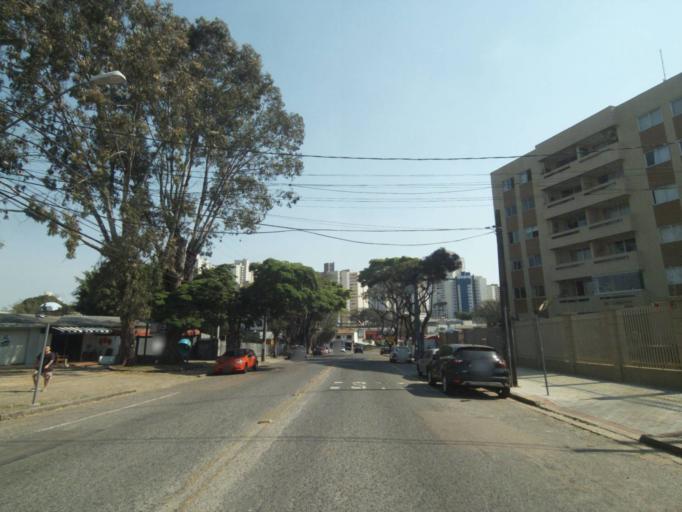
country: BR
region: Parana
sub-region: Curitiba
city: Curitiba
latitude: -25.4696
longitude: -49.2894
